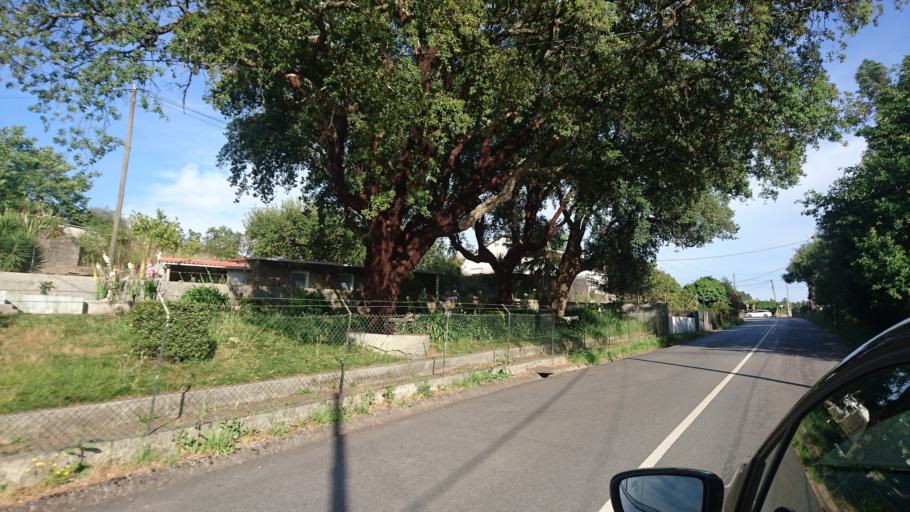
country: PT
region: Porto
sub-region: Paredes
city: Recarei
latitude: 41.1353
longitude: -8.3770
